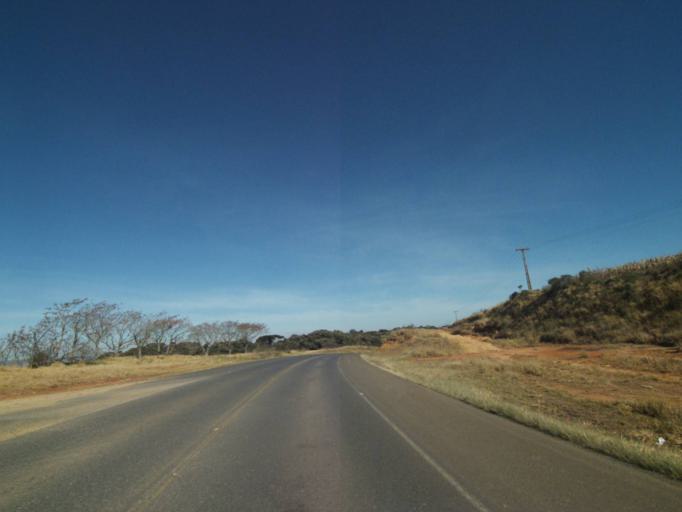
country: BR
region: Parana
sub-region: Tibagi
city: Tibagi
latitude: -24.3954
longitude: -50.3358
